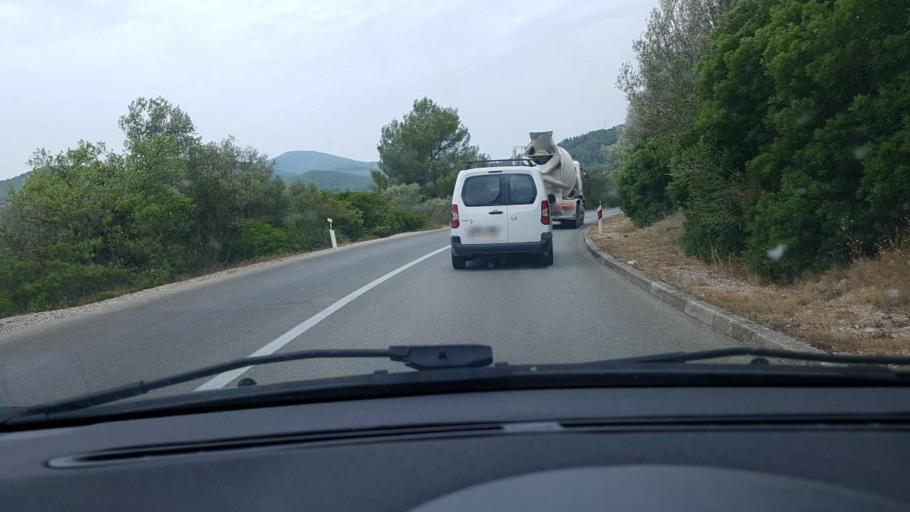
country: HR
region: Dubrovacko-Neretvanska
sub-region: Grad Dubrovnik
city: Vela Luka
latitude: 42.9481
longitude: 16.7632
